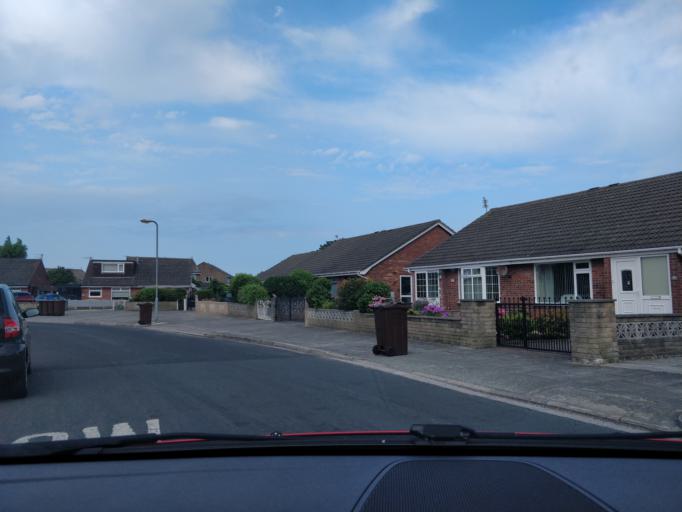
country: GB
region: England
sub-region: Lancashire
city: Banks
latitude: 53.6755
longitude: -2.9653
